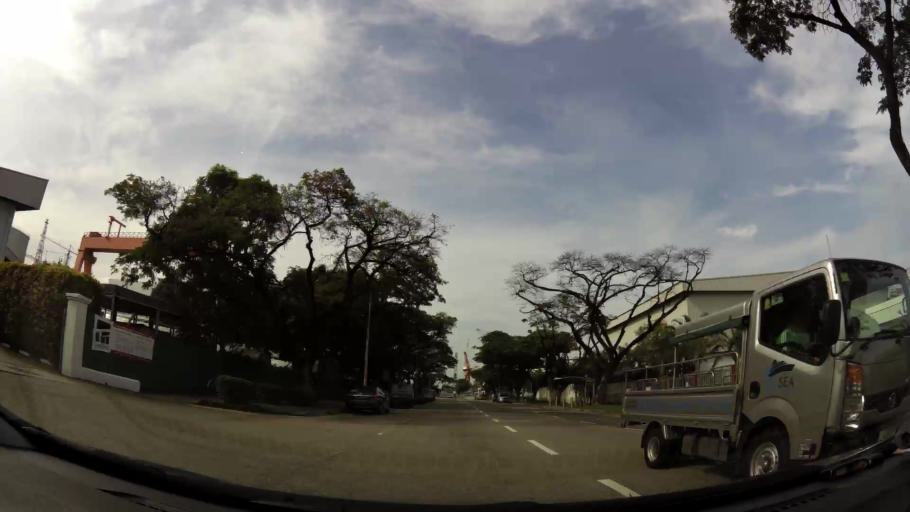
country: MY
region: Johor
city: Johor Bahru
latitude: 1.3087
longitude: 103.6504
